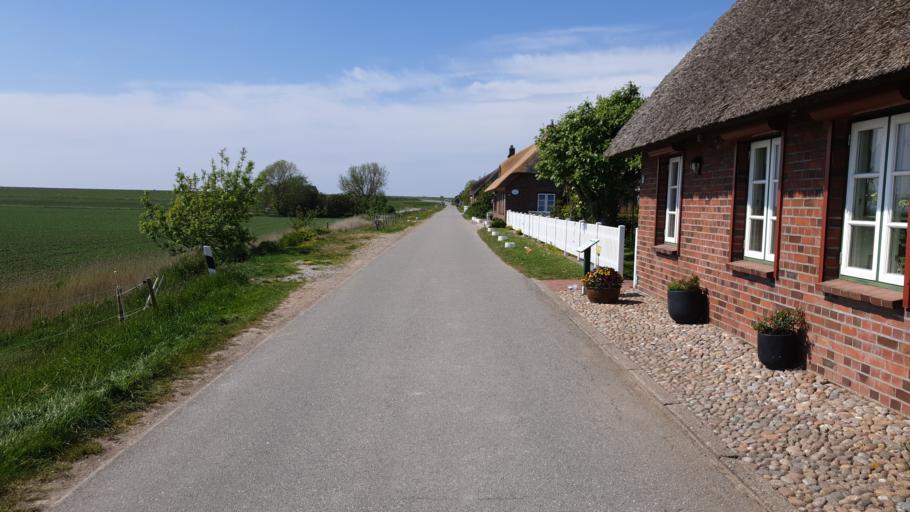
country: DE
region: Schleswig-Holstein
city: Elisabeth-Sophien-Koog
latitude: 54.5135
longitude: 8.8598
